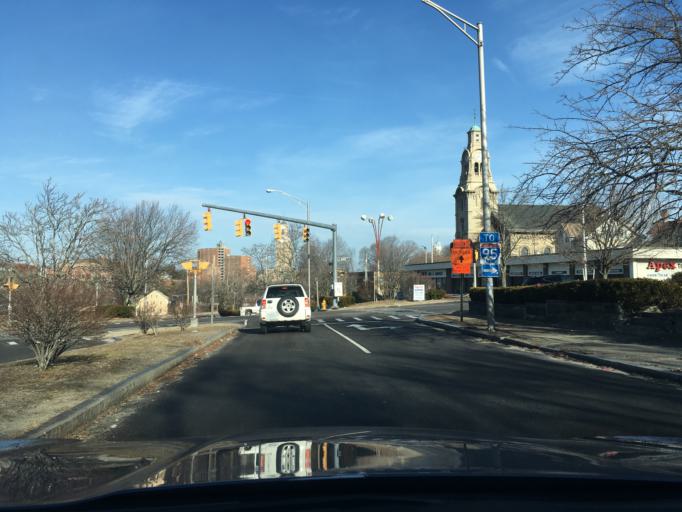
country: US
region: Rhode Island
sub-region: Providence County
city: Pawtucket
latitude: 41.8754
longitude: -71.3813
